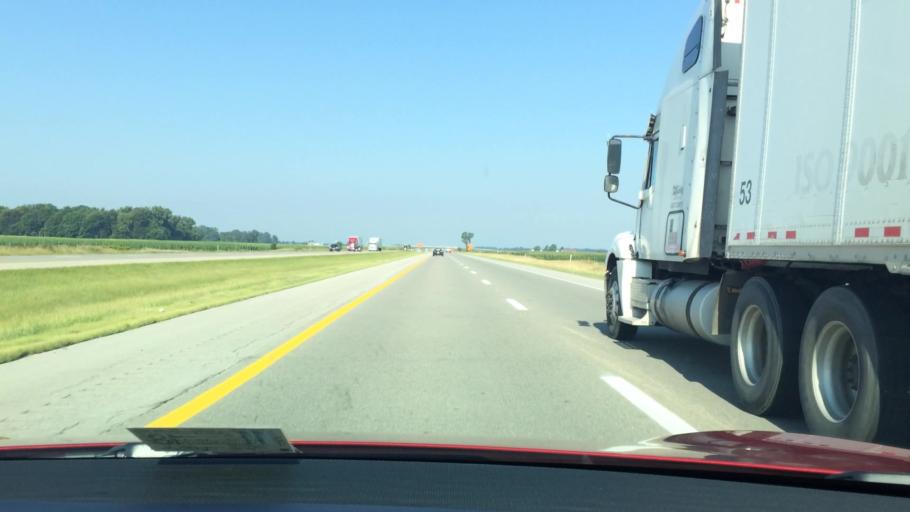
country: US
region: Ohio
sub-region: Fulton County
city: Burlington
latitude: 41.5908
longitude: -84.2364
